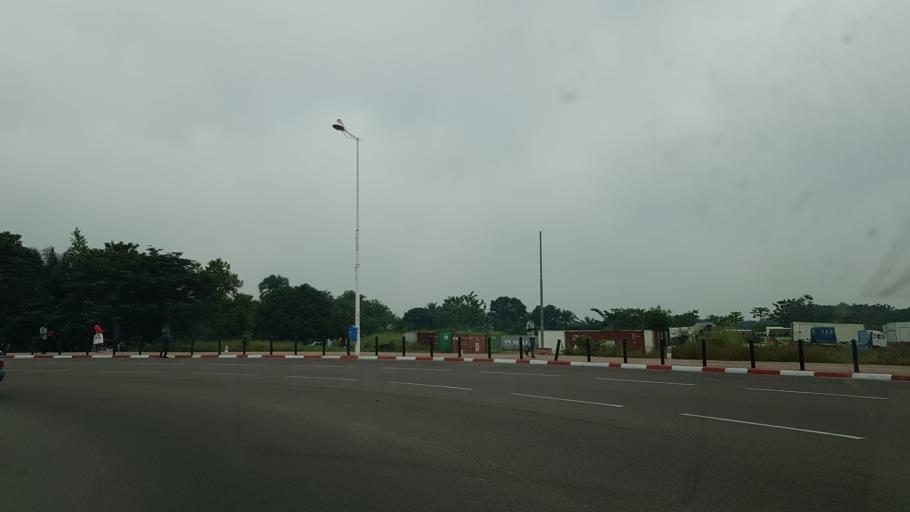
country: CG
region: Brazzaville
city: Brazzaville
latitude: -4.2614
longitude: 15.2519
